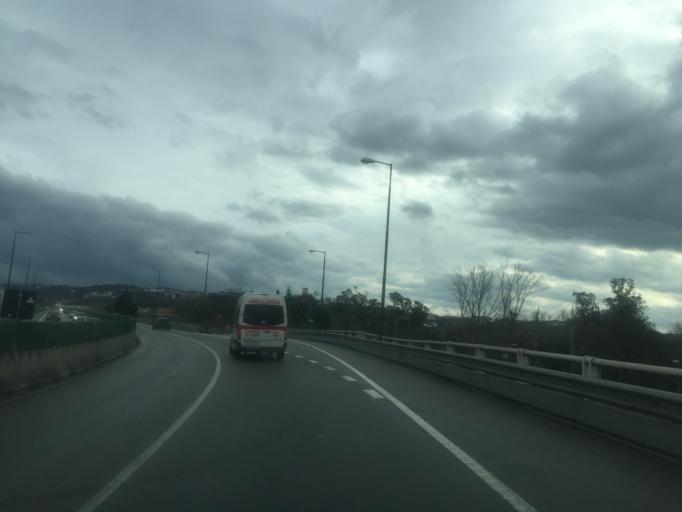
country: PT
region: Coimbra
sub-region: Coimbra
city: Coimbra
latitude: 40.2228
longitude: -8.4396
